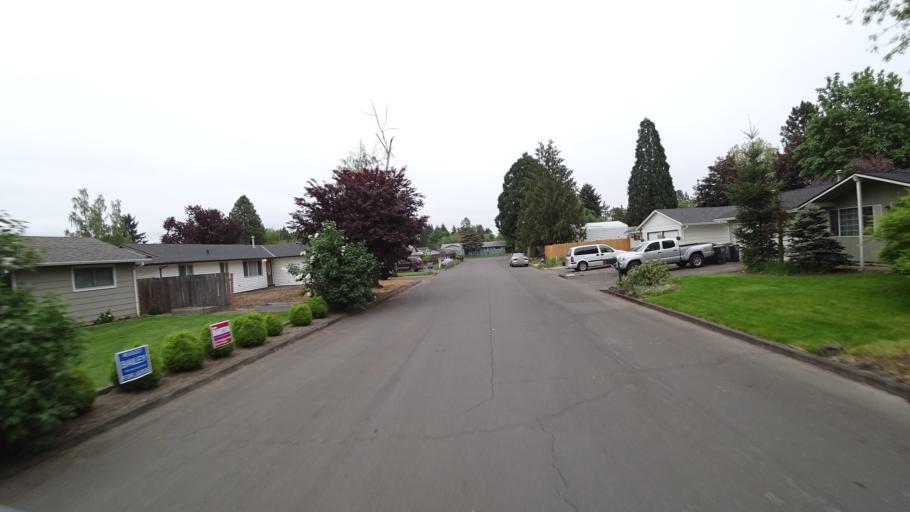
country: US
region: Oregon
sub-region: Washington County
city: Aloha
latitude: 45.5072
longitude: -122.8794
